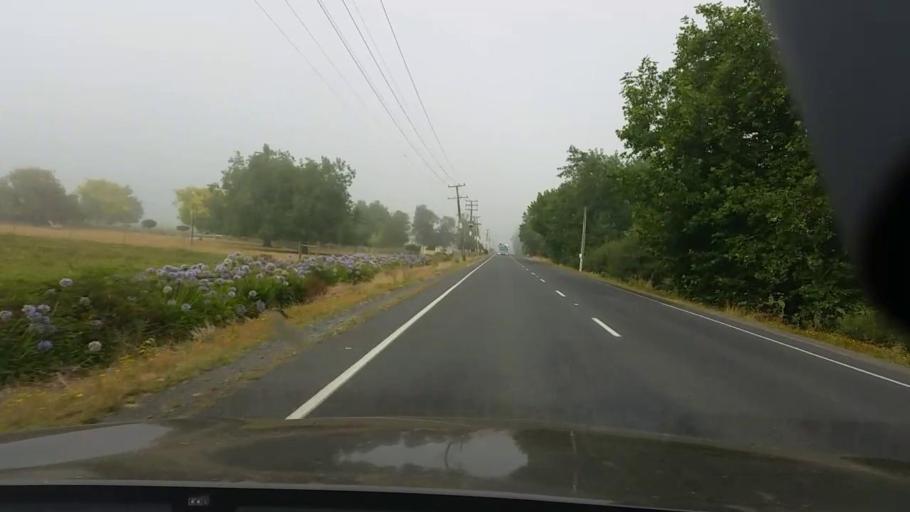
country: NZ
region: Waikato
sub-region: Hamilton City
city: Hamilton
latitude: -37.6306
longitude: 175.3124
